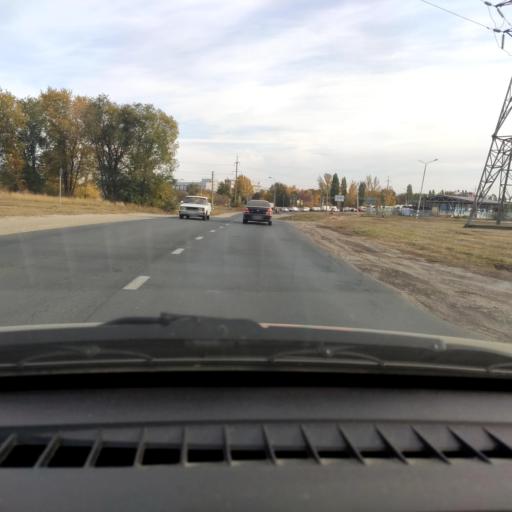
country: RU
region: Samara
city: Tol'yatti
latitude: 53.5664
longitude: 49.2885
